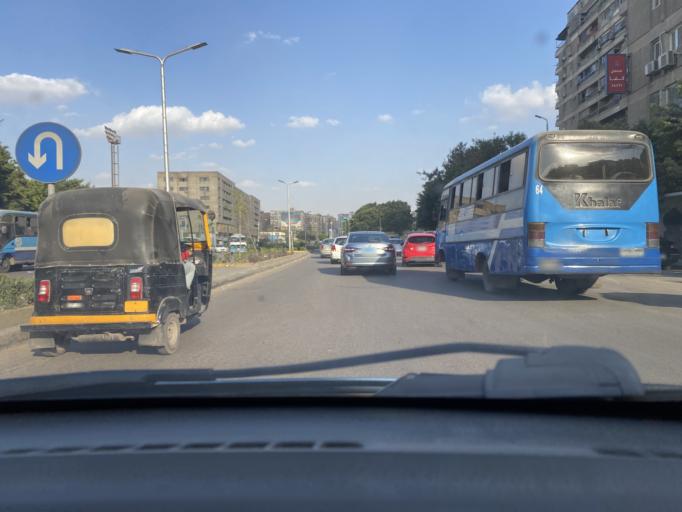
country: EG
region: Muhafazat al Qahirah
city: Cairo
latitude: 30.1032
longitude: 31.3001
